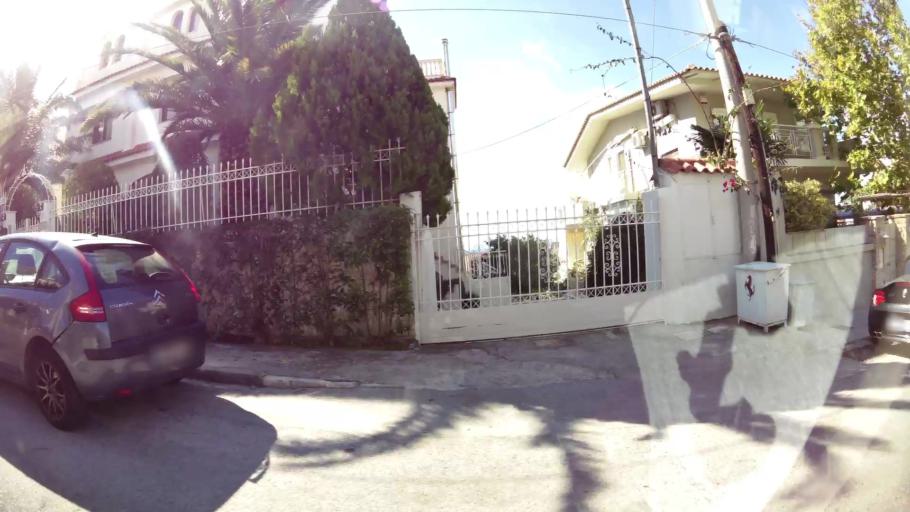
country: GR
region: Attica
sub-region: Nomarchia Anatolikis Attikis
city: Voula
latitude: 37.8498
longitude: 23.7792
